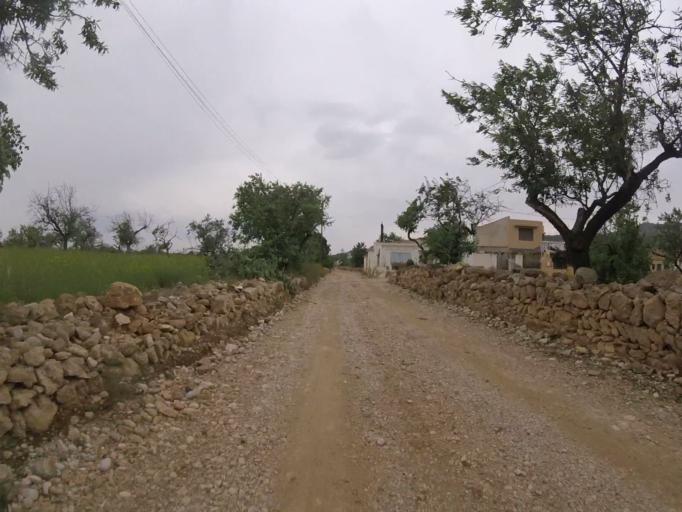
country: ES
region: Valencia
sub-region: Provincia de Castello
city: Alcoceber
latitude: 40.2418
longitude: 0.2676
